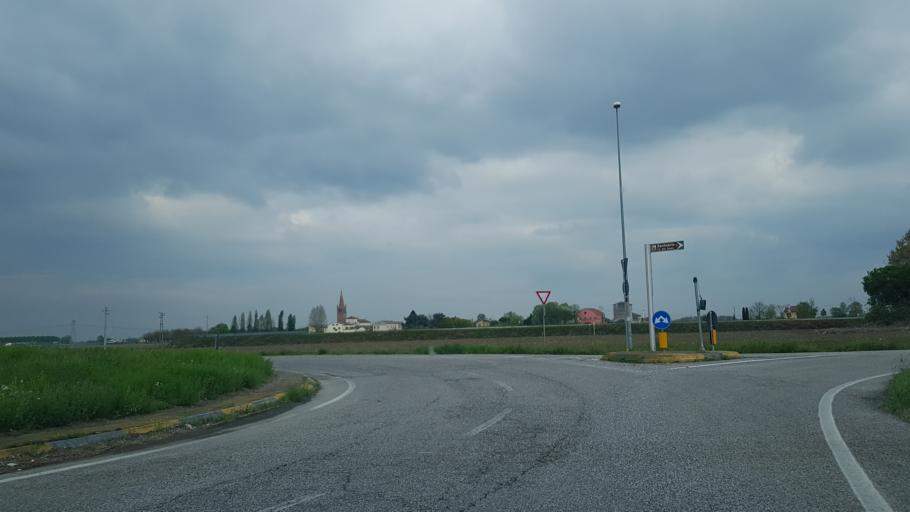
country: IT
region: Lombardy
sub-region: Provincia di Mantova
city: Ostiglia
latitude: 45.0871
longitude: 11.1560
